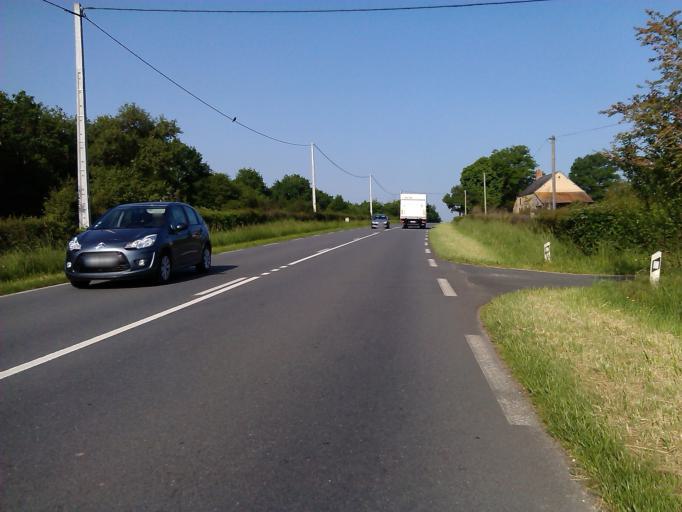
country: FR
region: Centre
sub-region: Departement de l'Indre
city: La Chatre
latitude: 46.5717
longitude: 1.9239
